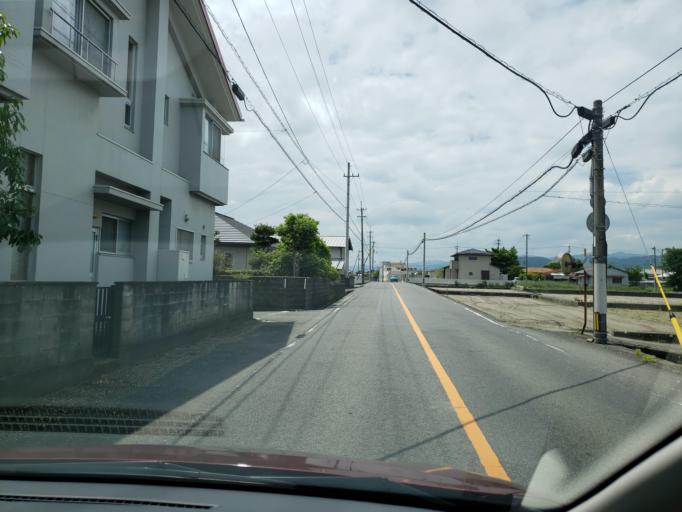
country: JP
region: Tokushima
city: Kamojimacho-jogejima
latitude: 34.0971
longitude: 134.3595
